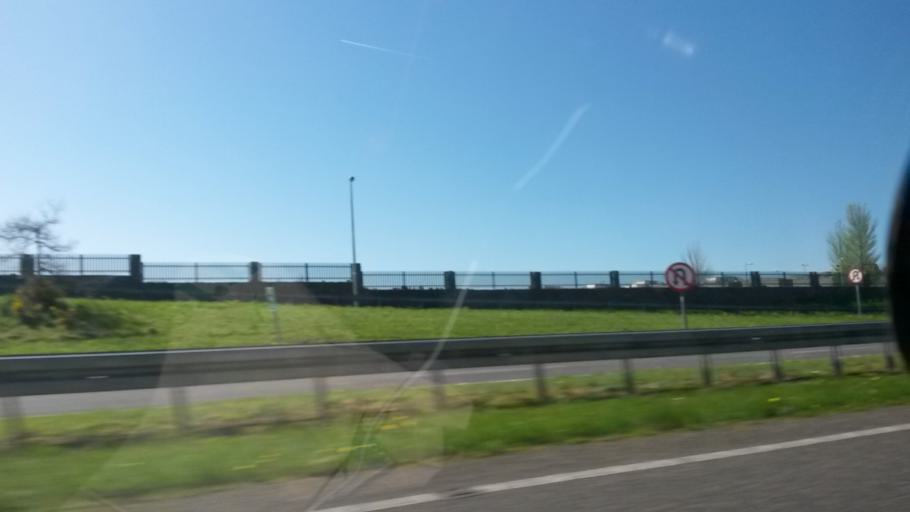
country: IE
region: Munster
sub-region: County Cork
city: Killumney
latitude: 51.8788
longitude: -8.6384
